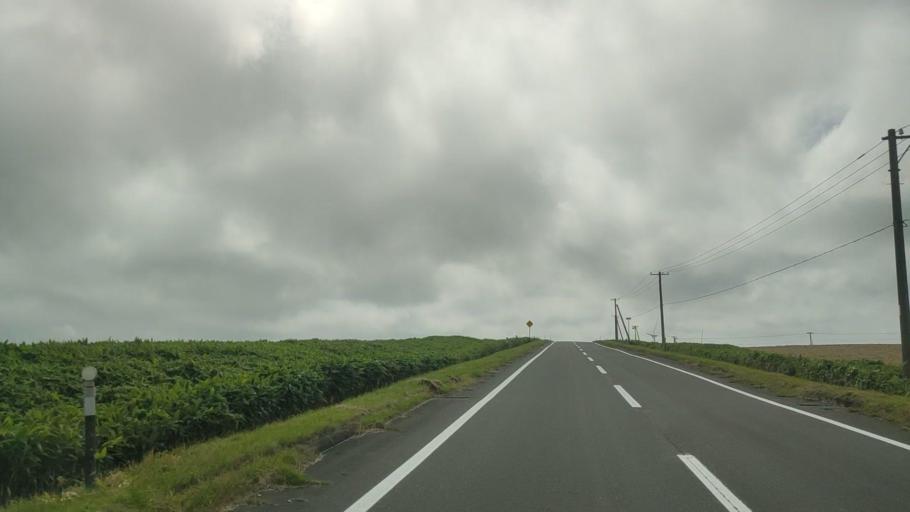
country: JP
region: Hokkaido
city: Makubetsu
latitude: 45.4889
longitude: 141.9378
